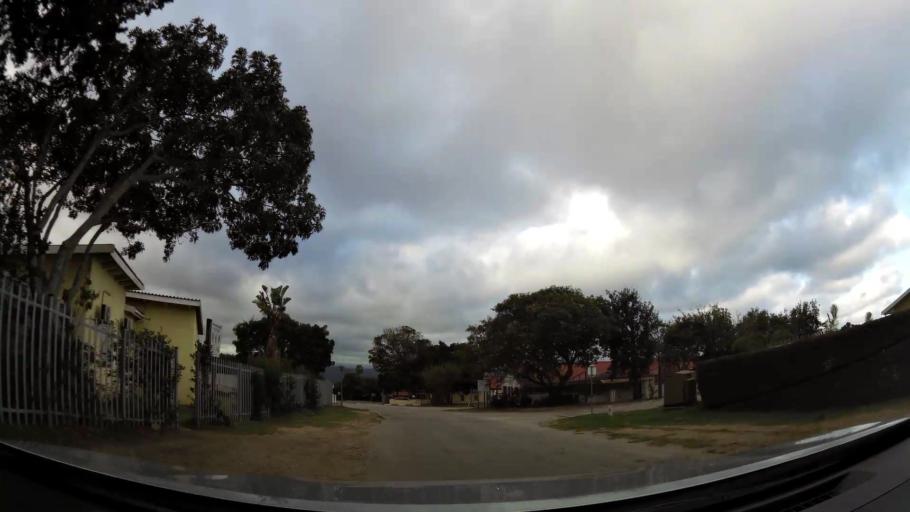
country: ZA
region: Western Cape
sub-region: Eden District Municipality
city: Plettenberg Bay
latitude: -34.0556
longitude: 23.3663
